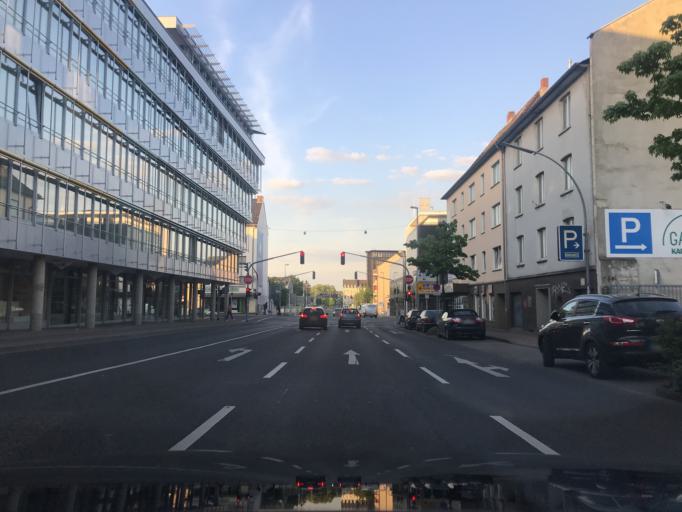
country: DE
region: North Rhine-Westphalia
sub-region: Regierungsbezirk Dusseldorf
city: Monchengladbach
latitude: 51.1964
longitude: 6.4401
